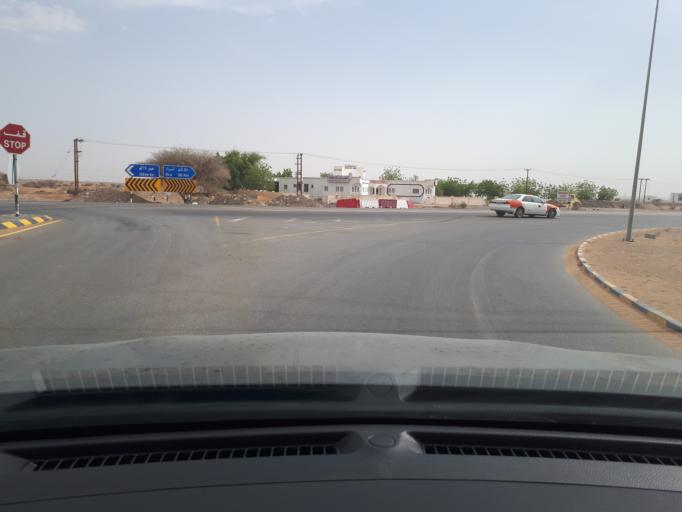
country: OM
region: Ash Sharqiyah
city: Badiyah
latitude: 22.4945
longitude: 58.9379
